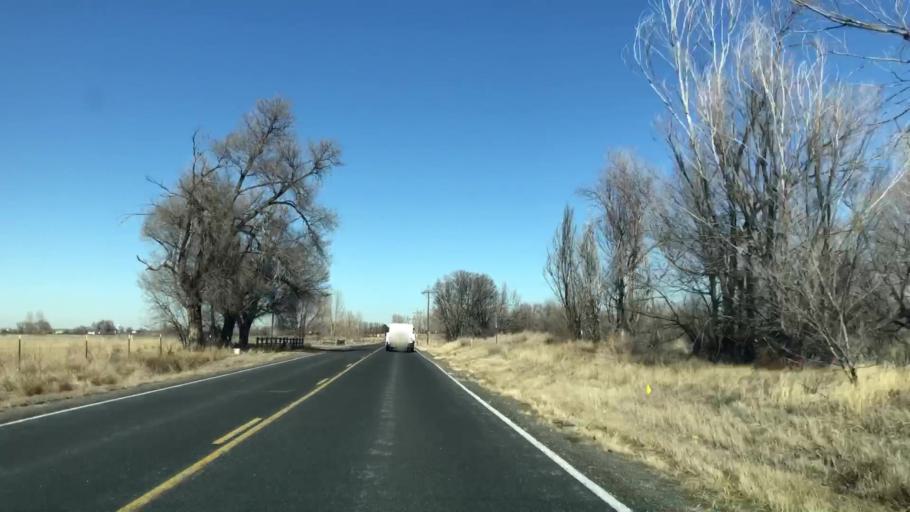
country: US
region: Colorado
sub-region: Weld County
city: Windsor
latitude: 40.4828
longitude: -104.9441
